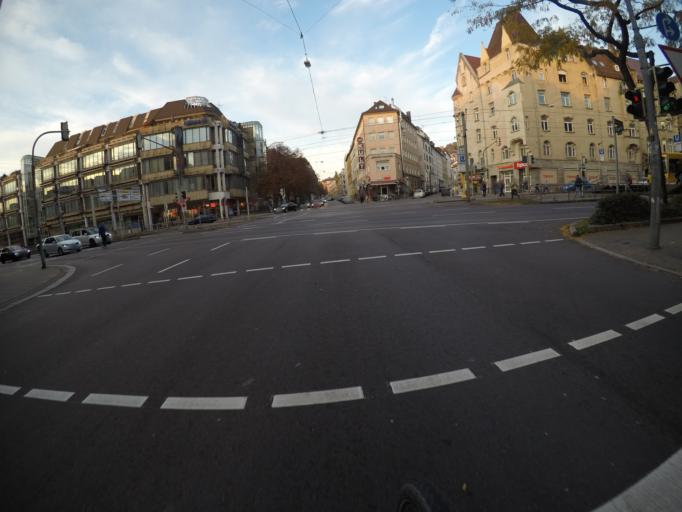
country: DE
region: Baden-Wuerttemberg
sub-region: Regierungsbezirk Stuttgart
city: Stuttgart
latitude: 48.7743
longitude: 9.1853
